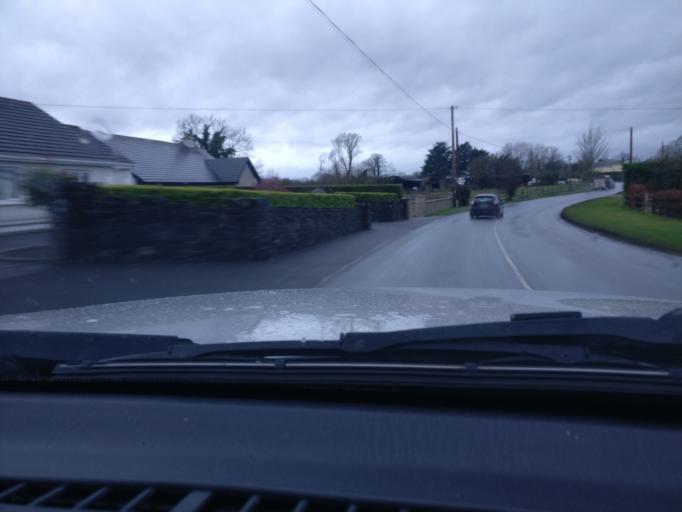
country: IE
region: Leinster
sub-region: An Mhi
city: Longwood
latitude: 53.4525
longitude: -6.9468
